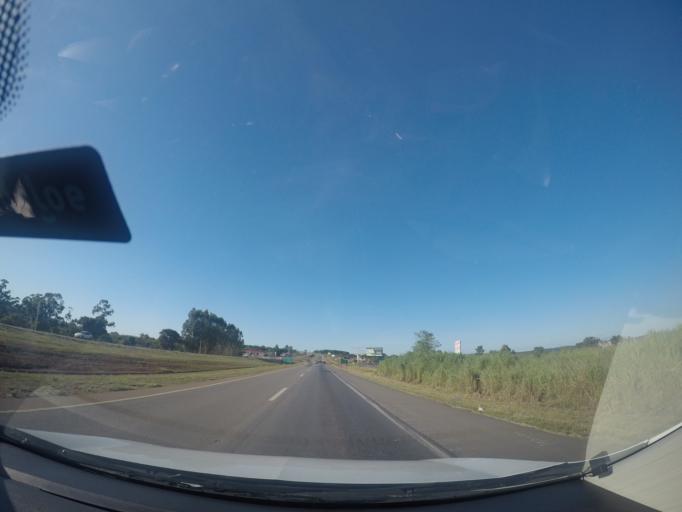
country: BR
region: Goias
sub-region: Aparecida De Goiania
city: Aparecida de Goiania
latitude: -16.8857
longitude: -49.2542
